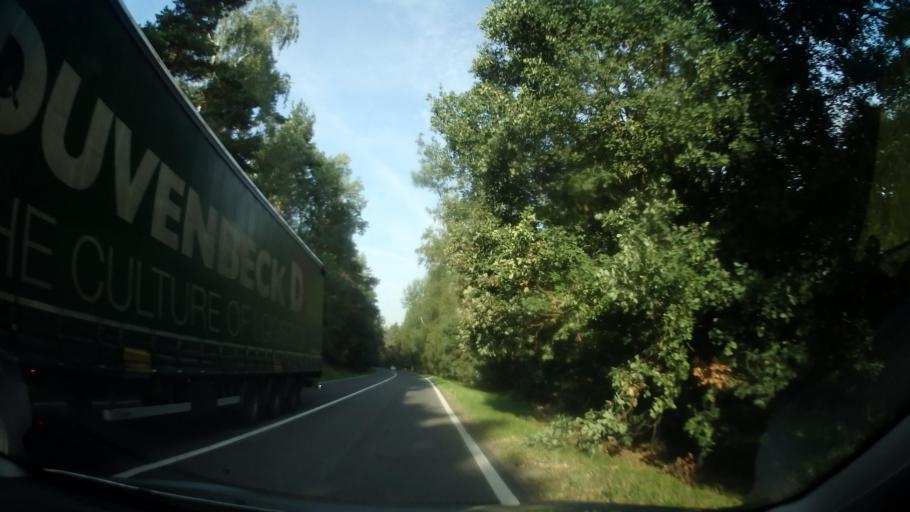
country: CZ
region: Jihocesky
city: Cimelice
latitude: 49.4379
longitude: 14.1374
